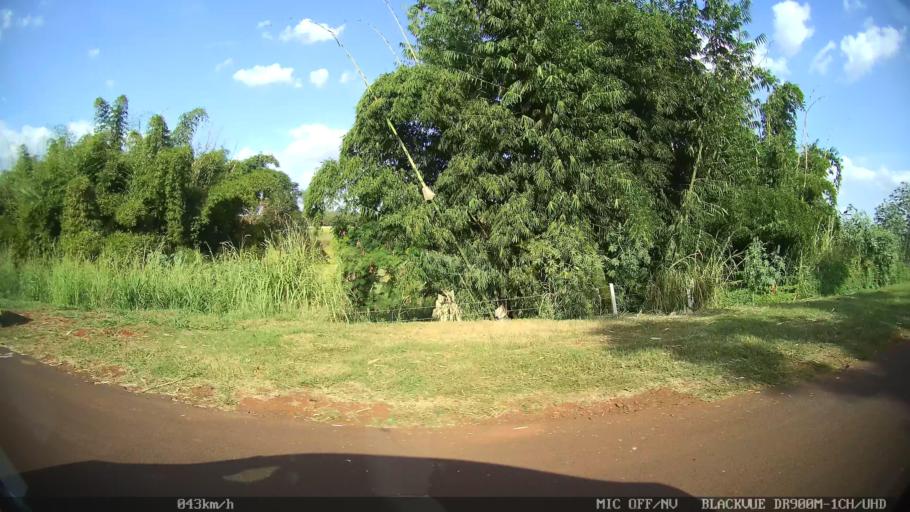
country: BR
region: Sao Paulo
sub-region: Ribeirao Preto
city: Ribeirao Preto
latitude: -21.1970
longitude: -47.8757
